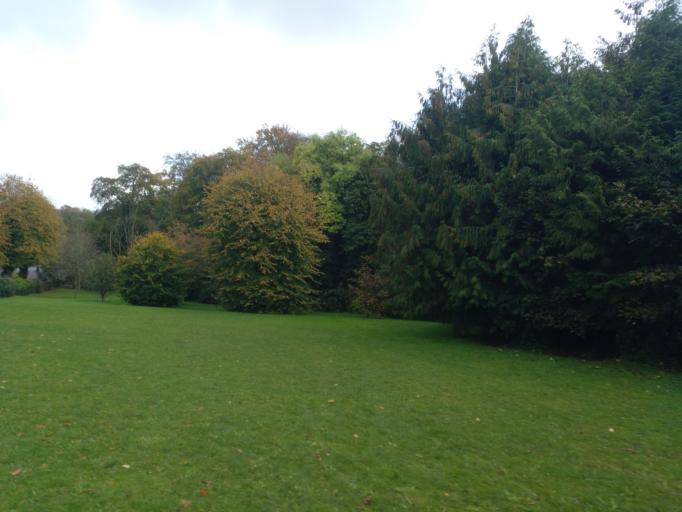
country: IE
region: Leinster
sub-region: Kilkenny
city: Castlecomer
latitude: 52.8054
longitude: -7.2071
